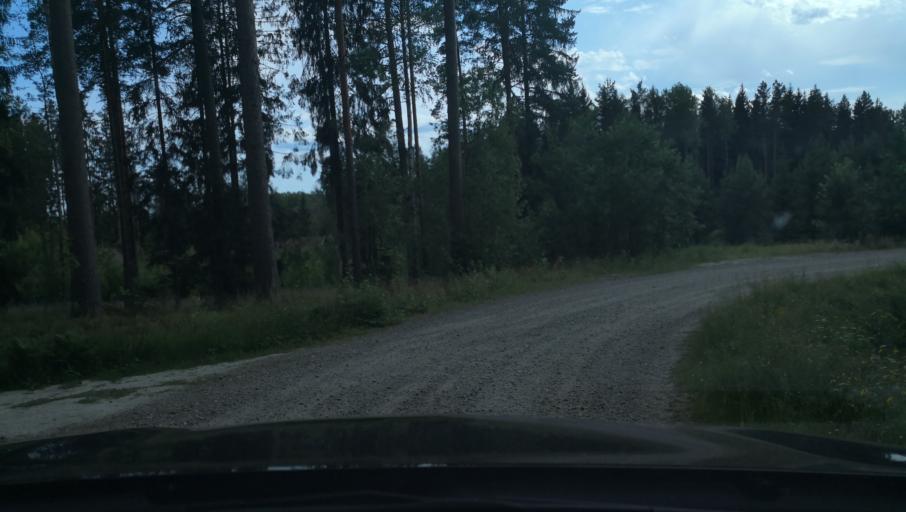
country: SE
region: Vaestmanland
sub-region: Norbergs Kommun
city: Norberg
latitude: 59.9833
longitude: 15.9497
